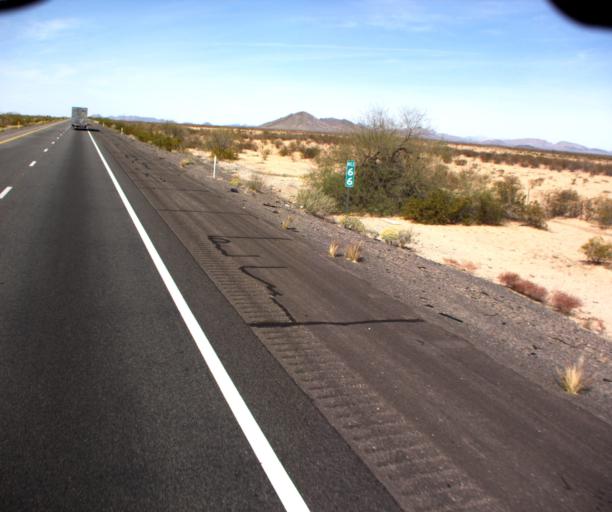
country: US
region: Arizona
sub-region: La Paz County
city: Salome
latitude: 33.5786
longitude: -113.4147
